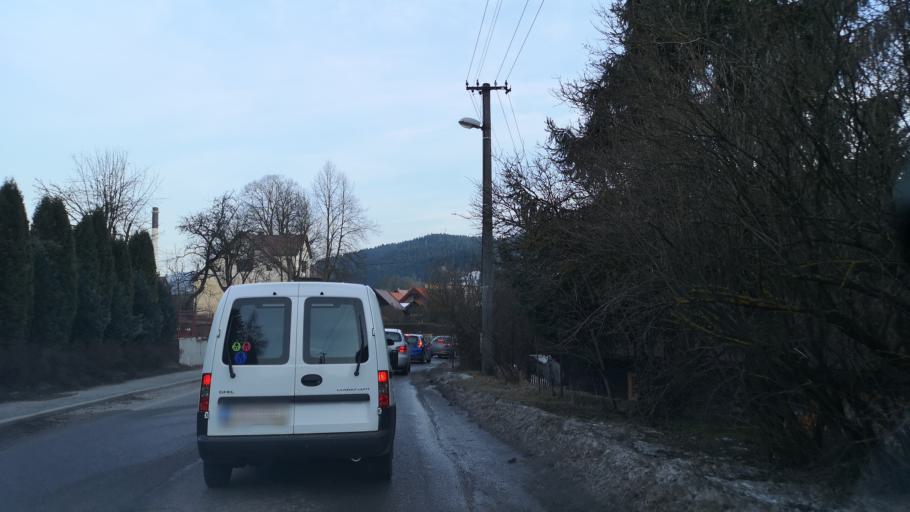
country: SK
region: Zilinsky
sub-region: Okres Dolny Kubin
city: Dolny Kubin
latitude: 49.2134
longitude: 19.2708
